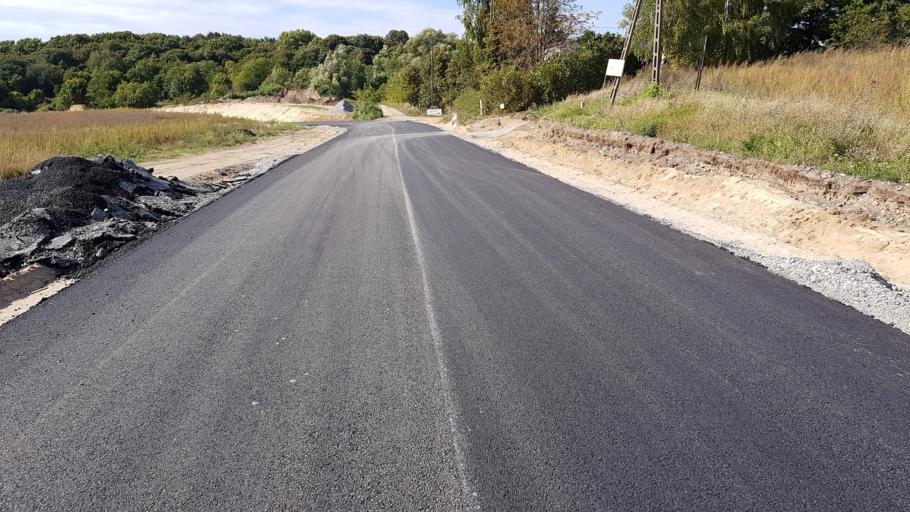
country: PL
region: West Pomeranian Voivodeship
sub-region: Powiat policki
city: Kolbaskowo
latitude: 53.3435
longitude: 14.4457
